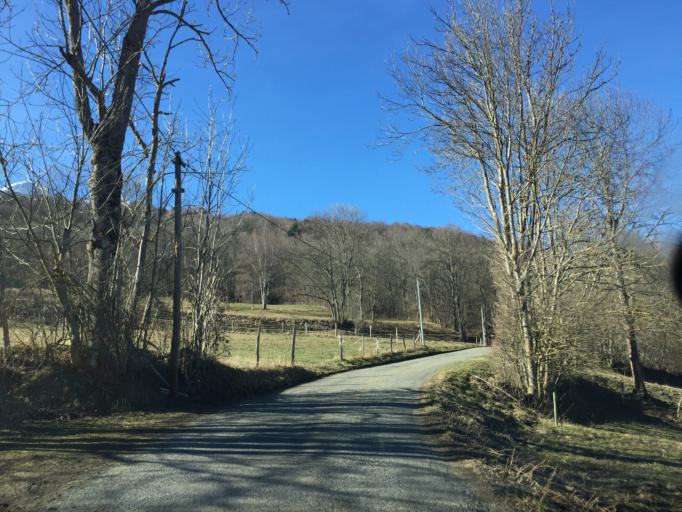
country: FR
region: Midi-Pyrenees
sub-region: Departement des Hautes-Pyrenees
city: Saint-Lary-Soulan
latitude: 42.8139
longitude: 0.3405
